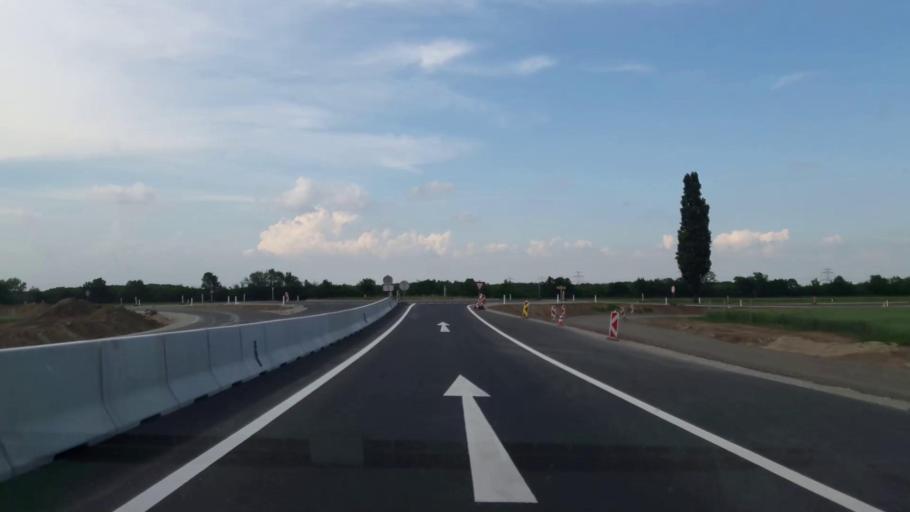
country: AT
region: Lower Austria
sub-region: Politischer Bezirk Wien-Umgebung
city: Fischamend Dorf
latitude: 48.1153
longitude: 16.6342
